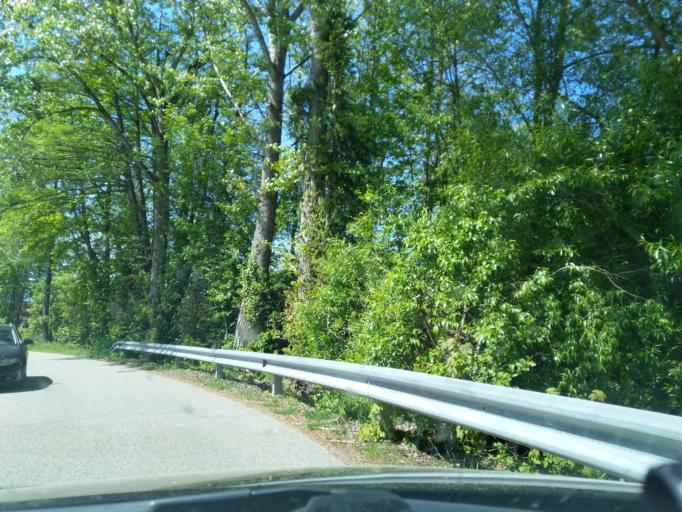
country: AT
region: Upper Austria
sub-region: Politischer Bezirk Ried im Innkreis
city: Ried im Innkreis
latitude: 48.2290
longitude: 13.4939
